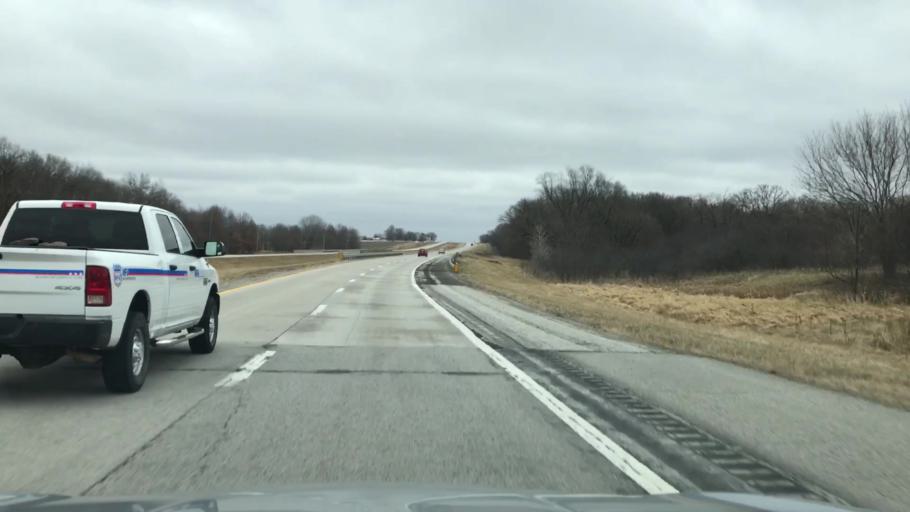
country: US
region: Missouri
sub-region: Livingston County
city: Chillicothe
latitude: 39.7773
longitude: -93.3625
